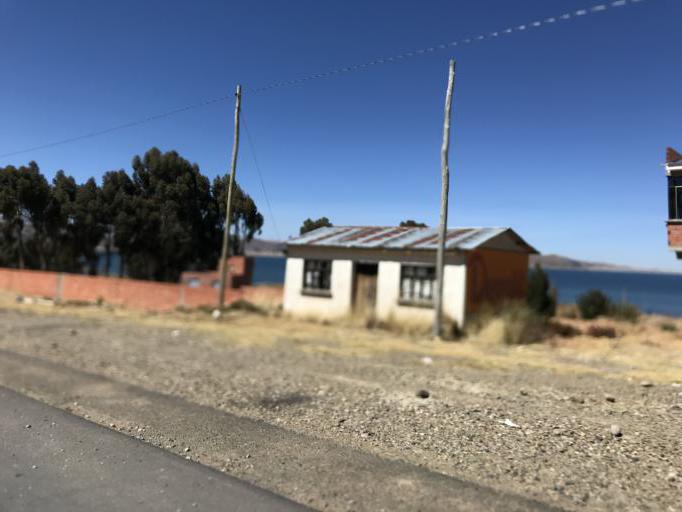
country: BO
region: La Paz
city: Huarina
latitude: -16.2159
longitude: -68.6458
